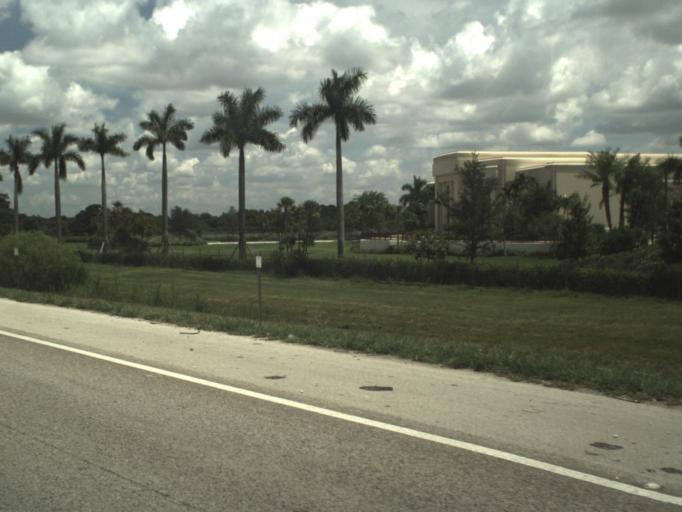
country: US
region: Florida
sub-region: Broward County
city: Southwest Ranches
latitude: 26.0694
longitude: -80.3566
